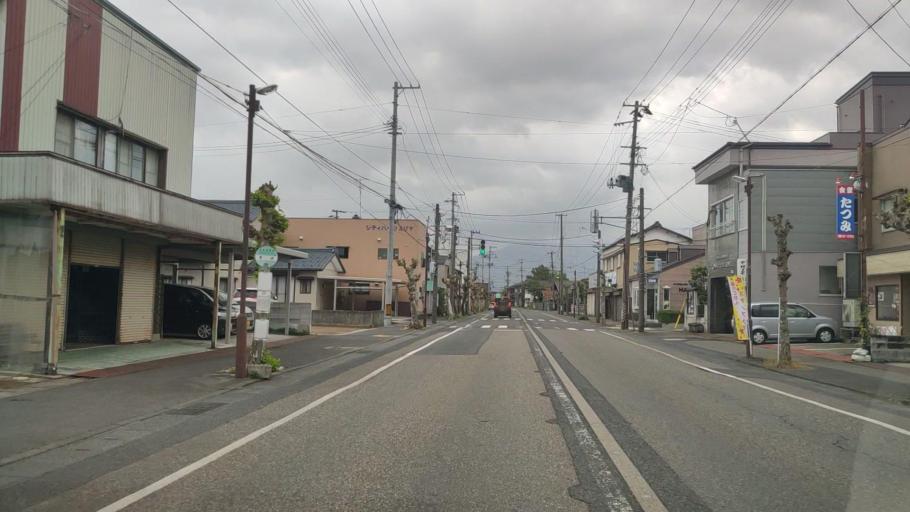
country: JP
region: Niigata
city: Gosen
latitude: 37.7371
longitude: 139.1843
